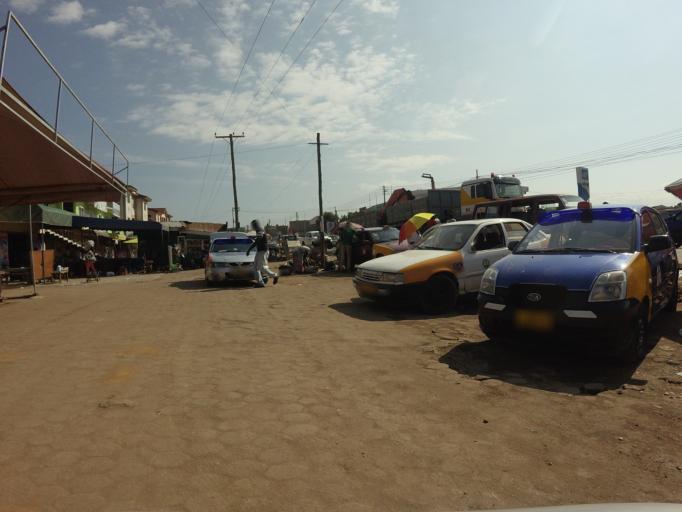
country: GH
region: Greater Accra
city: Dome
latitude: 5.6452
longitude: -0.2371
